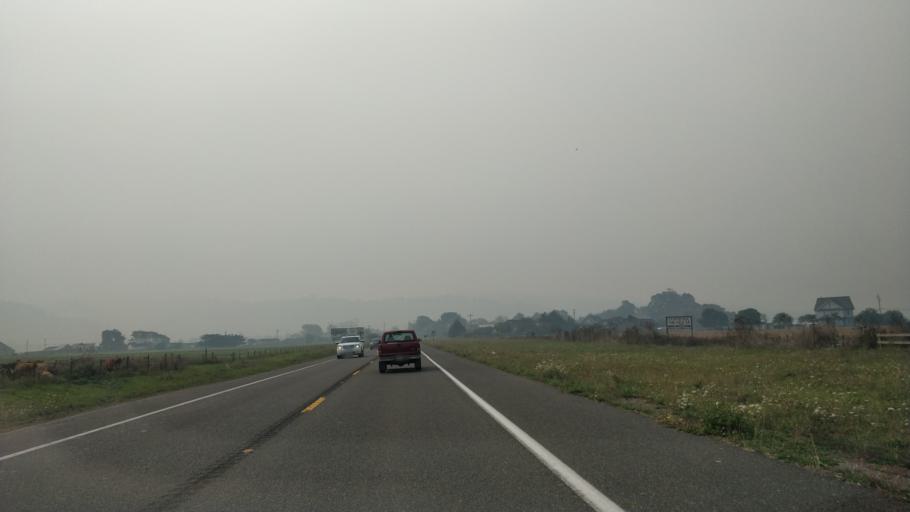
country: US
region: California
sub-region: Humboldt County
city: Ferndale
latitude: 40.5926
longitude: -124.2509
